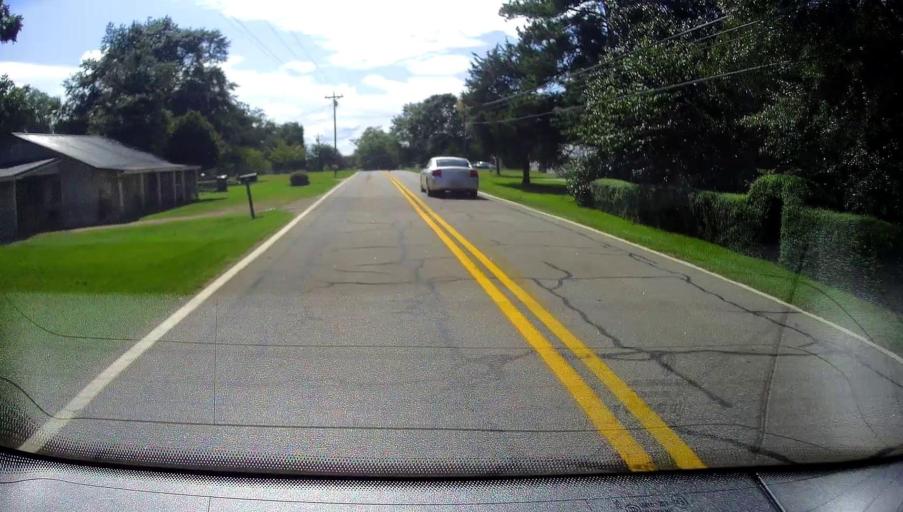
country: US
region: Georgia
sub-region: Upson County
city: Hannahs Mill
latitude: 32.9350
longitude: -84.3497
